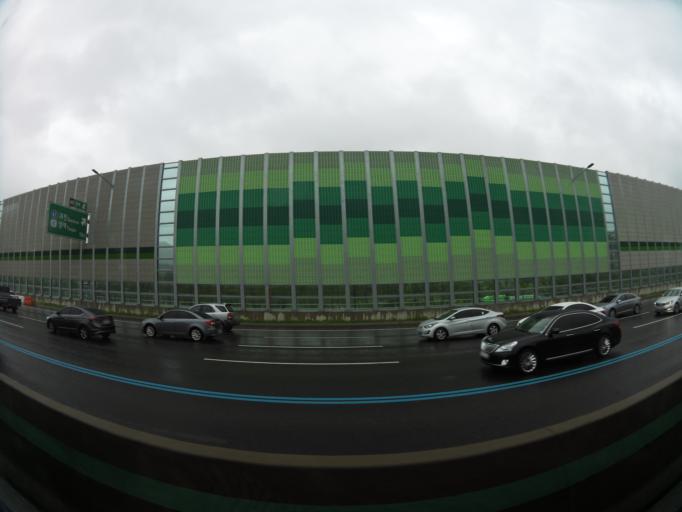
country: KR
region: Gyeonggi-do
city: Seongnam-si
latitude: 37.4502
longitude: 127.0523
